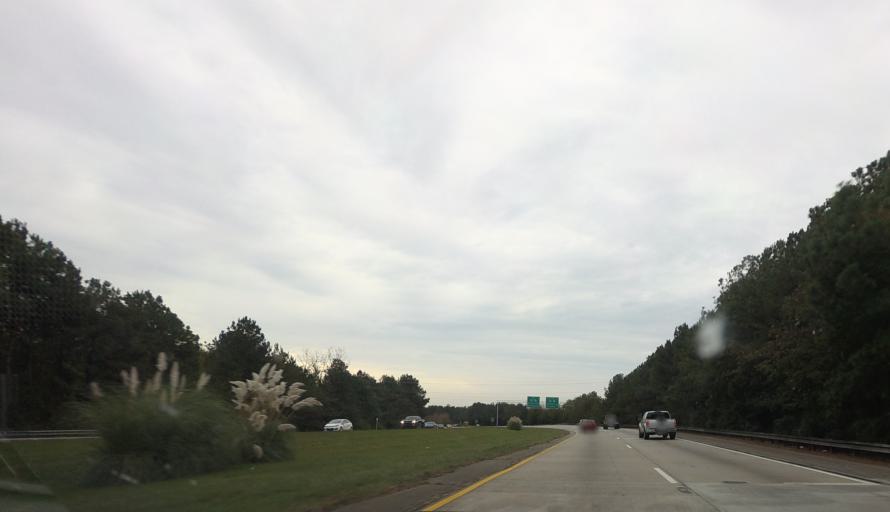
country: US
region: Alabama
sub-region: Russell County
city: Phenix City
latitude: 32.5180
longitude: -84.9924
